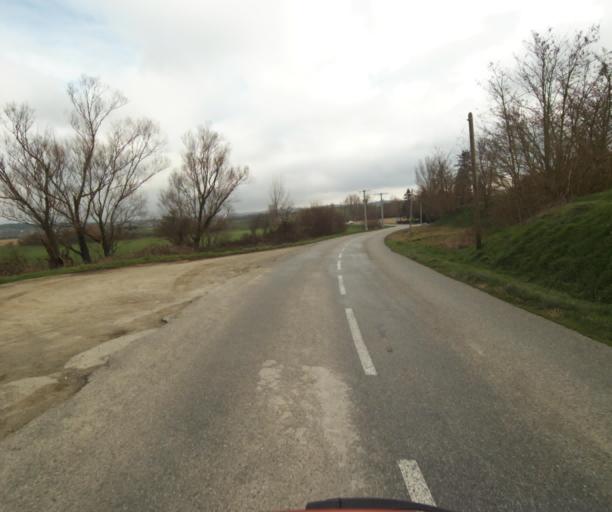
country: FR
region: Languedoc-Roussillon
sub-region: Departement de l'Aude
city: Belpech
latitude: 43.2128
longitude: 1.7252
